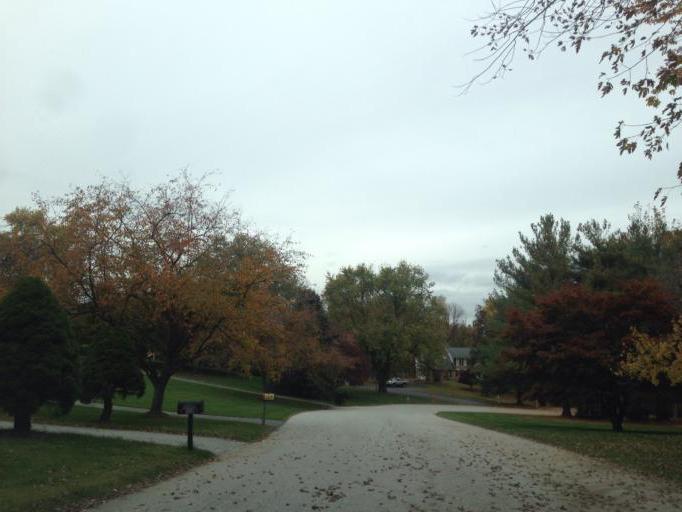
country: US
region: Maryland
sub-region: Howard County
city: Ellicott City
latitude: 39.3046
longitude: -76.8279
